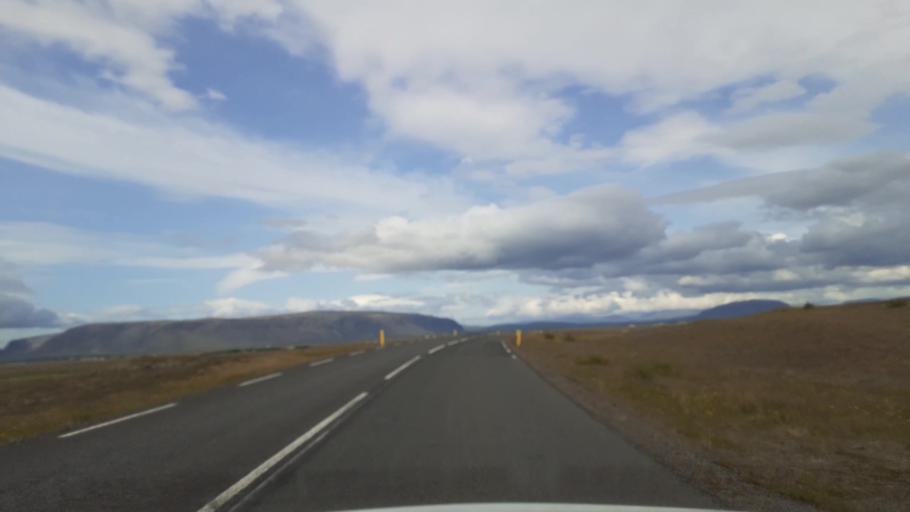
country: IS
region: South
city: Selfoss
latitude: 63.9202
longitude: -20.8493
